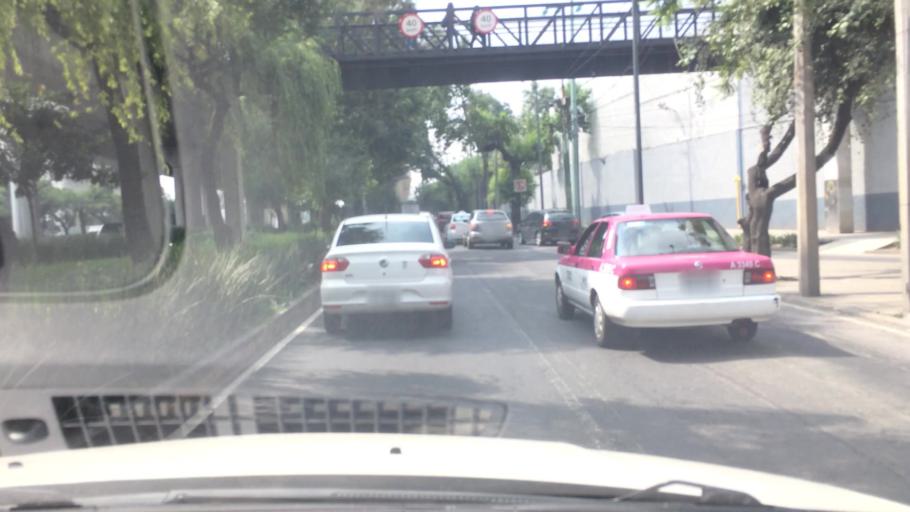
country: MX
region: Mexico City
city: Tlalpan
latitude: 19.2887
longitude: -99.1507
